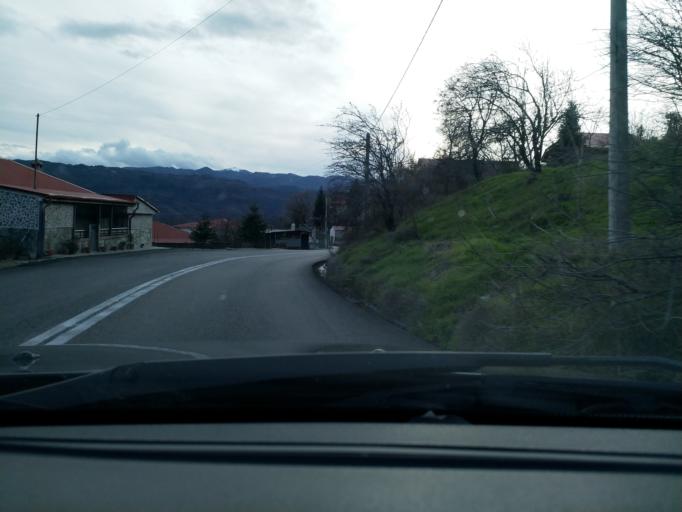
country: GR
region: Thessaly
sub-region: Trikala
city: Kastraki
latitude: 39.7879
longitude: 21.4091
